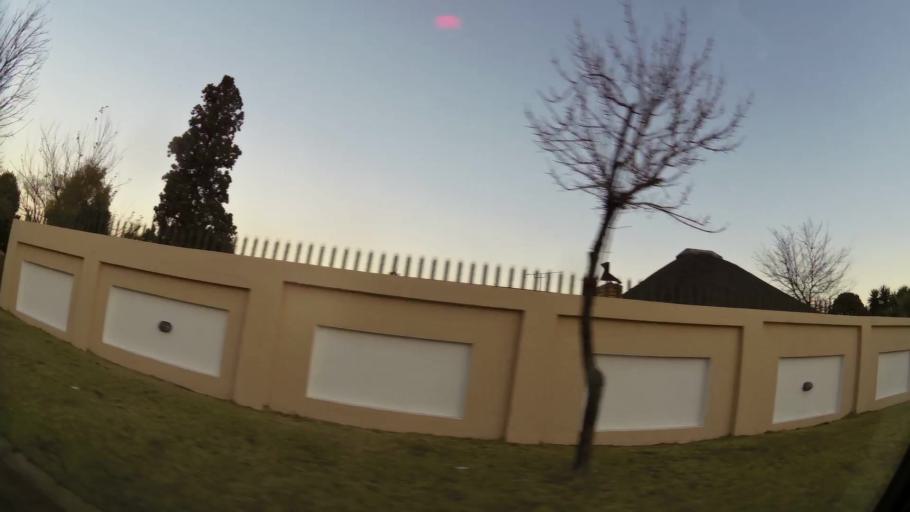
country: ZA
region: Gauteng
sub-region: Ekurhuleni Metropolitan Municipality
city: Germiston
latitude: -26.2638
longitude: 28.1582
